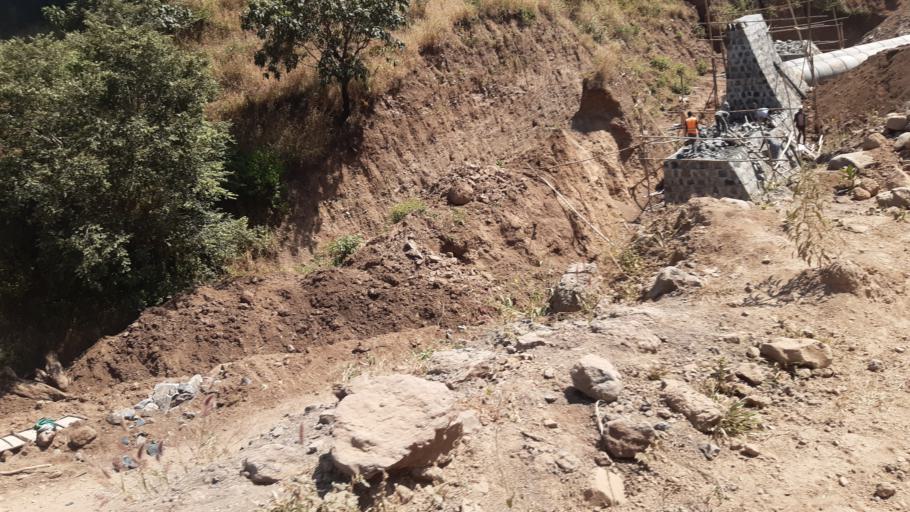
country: ET
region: Amhara
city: Dabat
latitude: 13.1925
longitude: 37.5720
